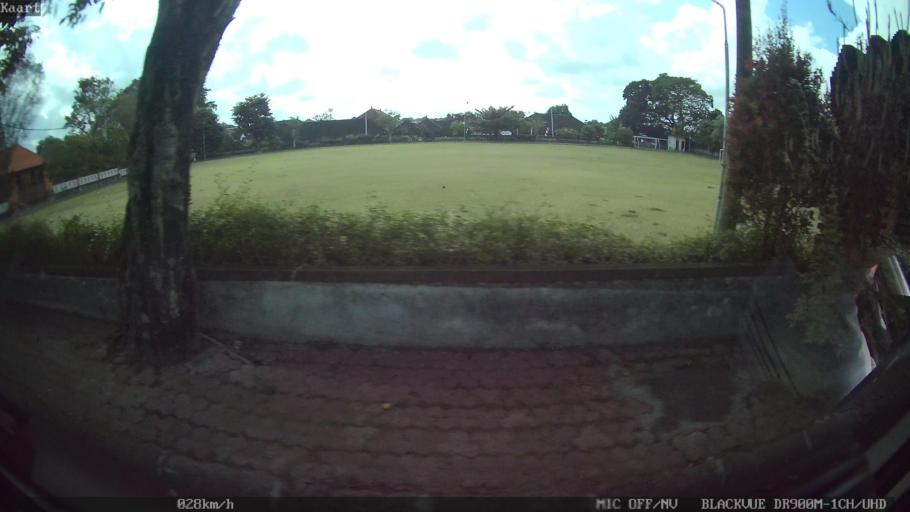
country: ID
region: Bali
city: Banjar Kertasari
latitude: -8.6245
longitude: 115.2036
